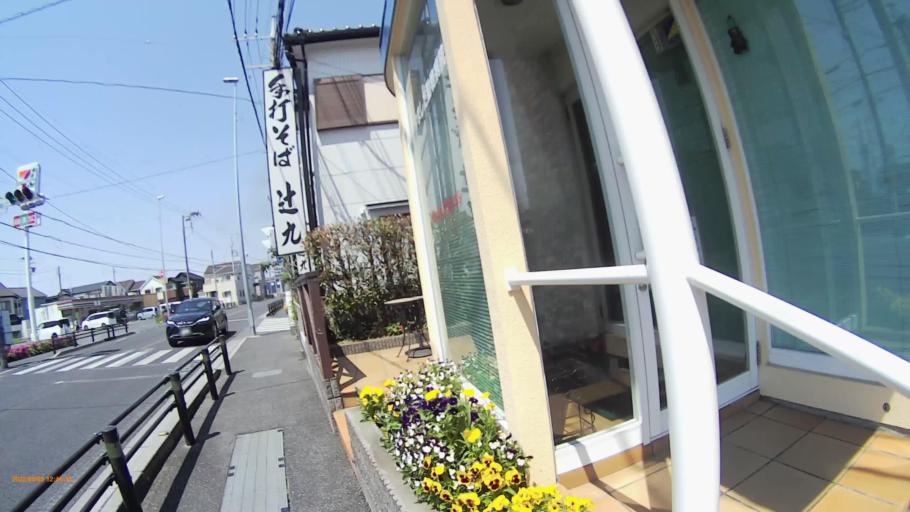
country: JP
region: Saitama
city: Kasukabe
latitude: 35.9494
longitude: 139.7757
